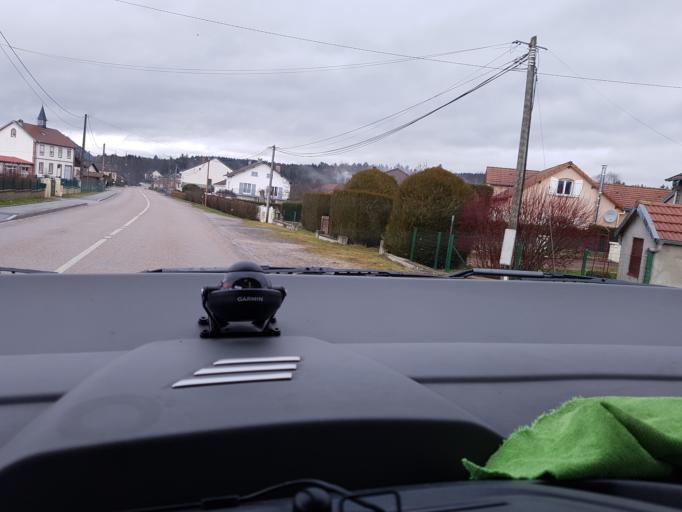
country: FR
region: Lorraine
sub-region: Departement des Vosges
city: Saint-Michel-sur-Meurthe
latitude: 48.3457
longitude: 6.8912
